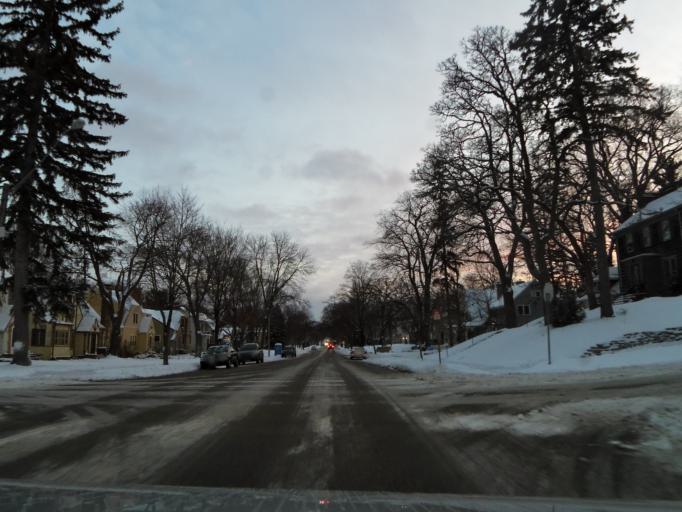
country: US
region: Minnesota
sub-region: Hennepin County
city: Saint Louis Park
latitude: 44.9289
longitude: -93.3215
